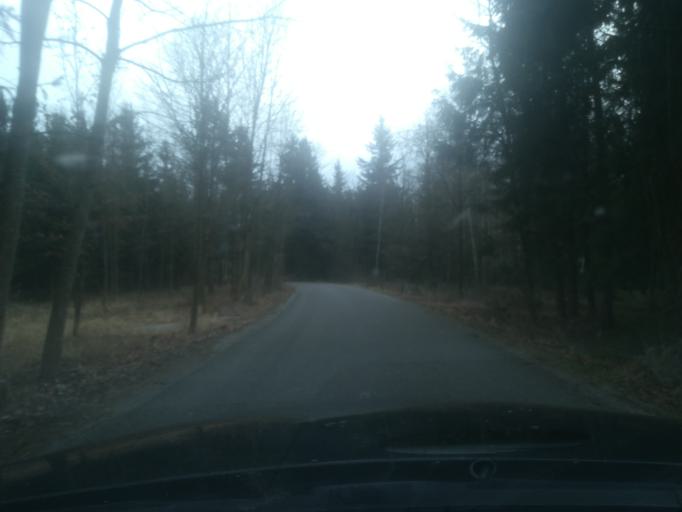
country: AT
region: Upper Austria
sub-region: Wels-Land
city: Gunskirchen
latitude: 48.1159
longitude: 13.9383
